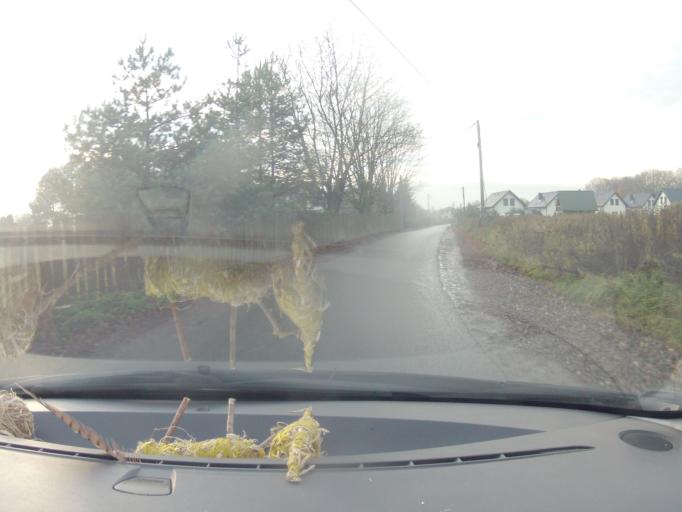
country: PL
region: Lesser Poland Voivodeship
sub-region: Krakow
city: Sidzina
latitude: 49.9979
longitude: 19.8824
